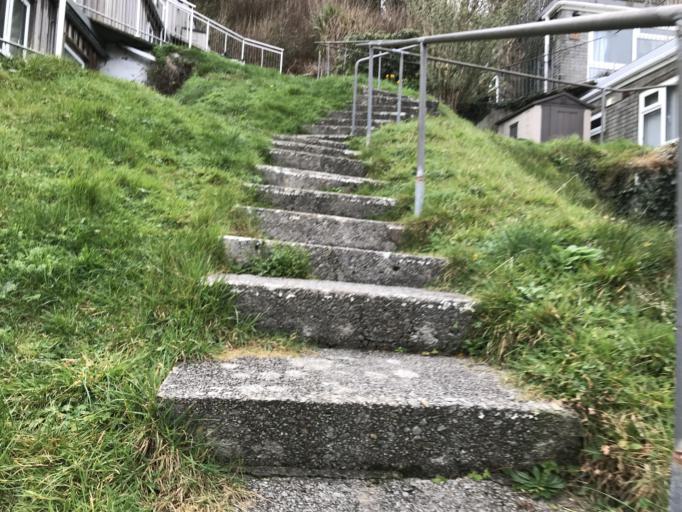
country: GB
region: England
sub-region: Cornwall
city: Looe
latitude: 50.3632
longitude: -4.4366
